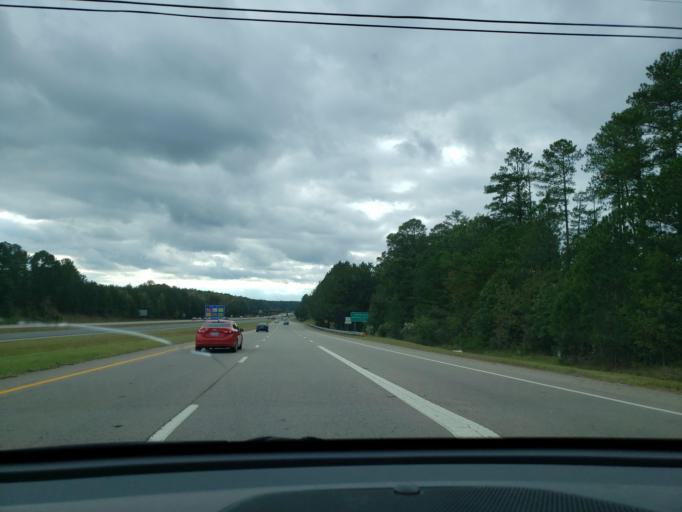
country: US
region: North Carolina
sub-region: Wake County
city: Morrisville
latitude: 35.9040
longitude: -78.7760
